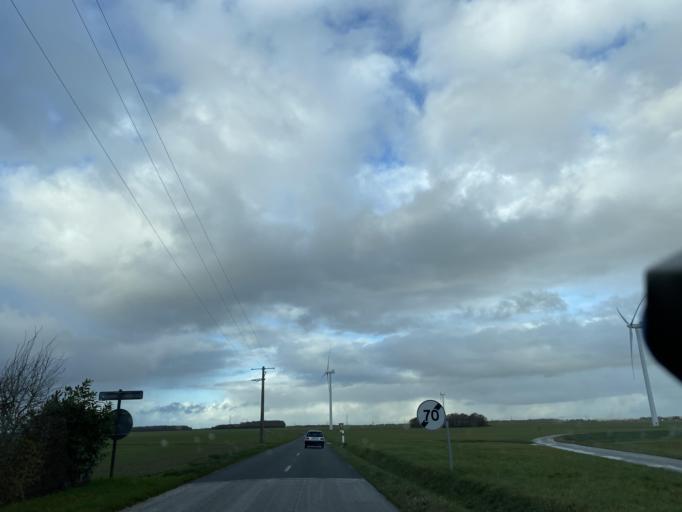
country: FR
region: Haute-Normandie
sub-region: Departement de l'Eure
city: Damville
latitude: 48.8380
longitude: 1.0639
